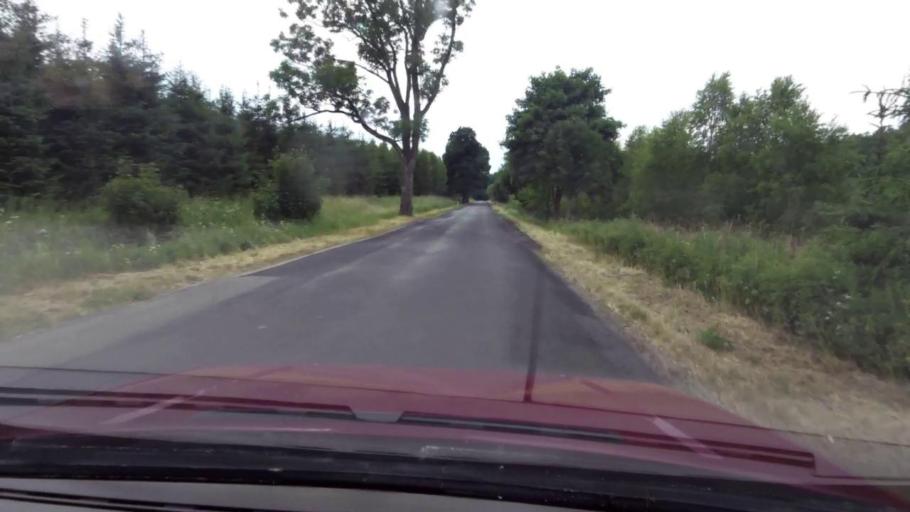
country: PL
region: Pomeranian Voivodeship
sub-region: Powiat bytowski
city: Trzebielino
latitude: 54.2677
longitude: 17.0296
